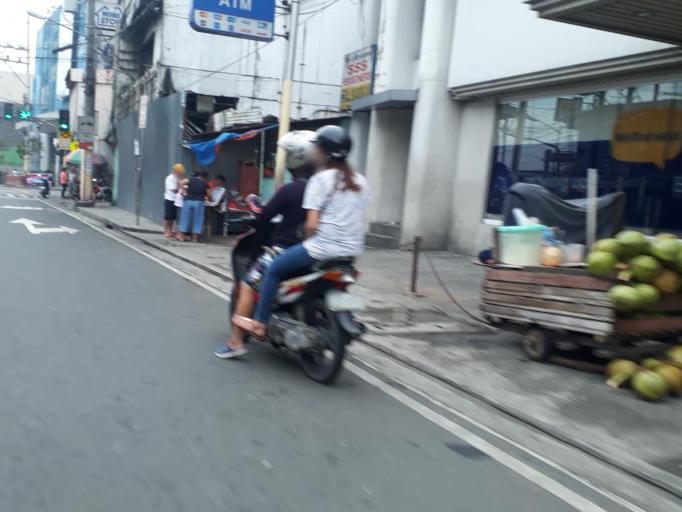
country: PH
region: Metro Manila
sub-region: Caloocan City
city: Niugan
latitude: 14.6575
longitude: 120.9715
